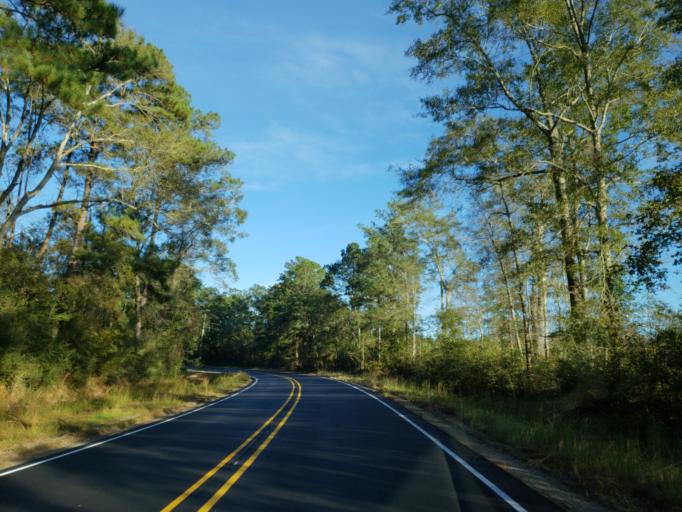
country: US
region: Mississippi
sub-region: Perry County
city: Richton
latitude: 31.3469
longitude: -88.7756
